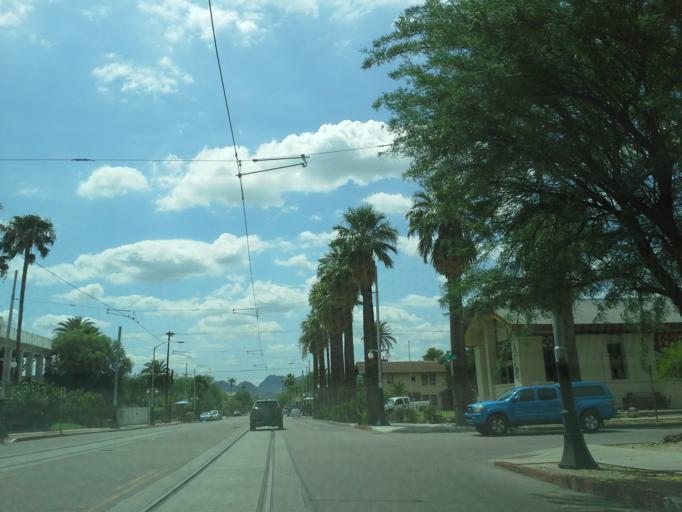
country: US
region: Arizona
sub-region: Pima County
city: South Tucson
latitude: 32.2317
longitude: -110.9607
